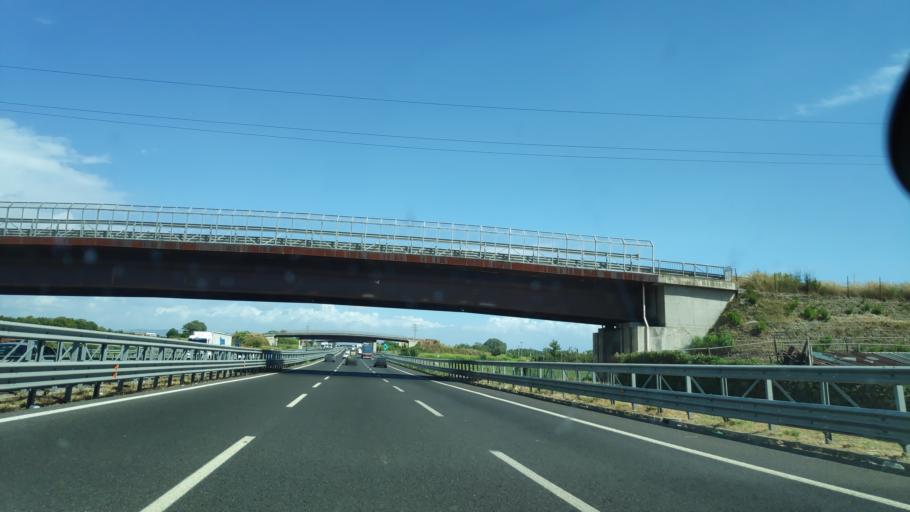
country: IT
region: Campania
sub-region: Provincia di Salerno
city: Pontecagnano
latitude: 40.6515
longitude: 14.8758
